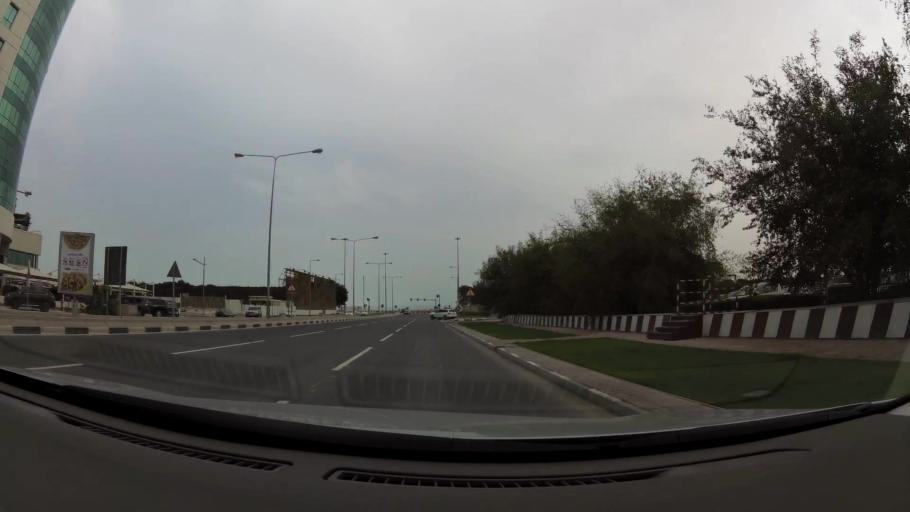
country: QA
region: Baladiyat ad Dawhah
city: Doha
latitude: 25.3124
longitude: 51.5187
